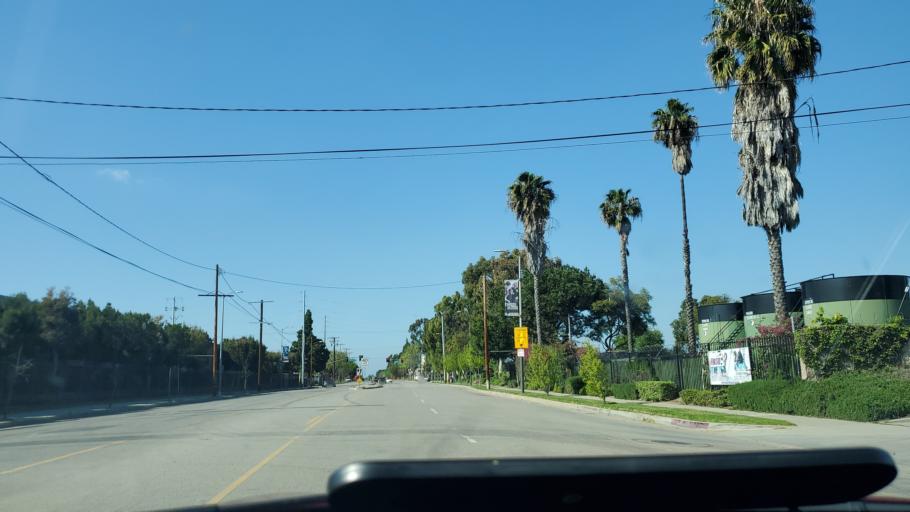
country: US
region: California
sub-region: Los Angeles County
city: West Carson
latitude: 33.7964
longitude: -118.2828
